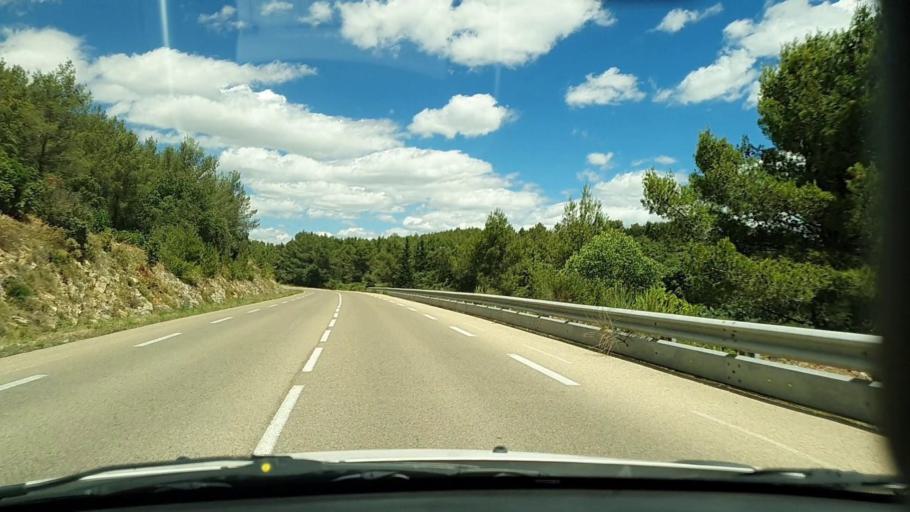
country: FR
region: Languedoc-Roussillon
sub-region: Departement du Gard
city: Poulx
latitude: 43.8804
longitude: 4.4173
